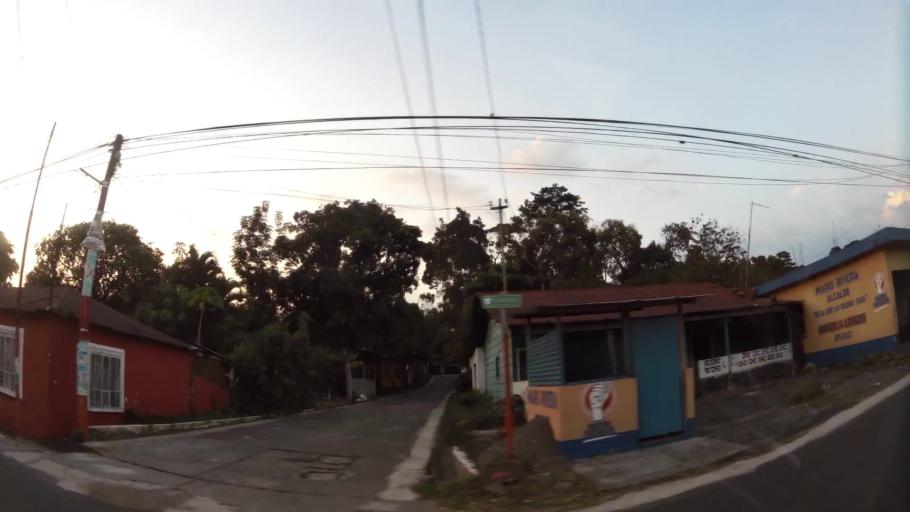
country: GT
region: Retalhuleu
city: Santa Cruz Mulua
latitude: 14.5799
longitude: -91.6257
